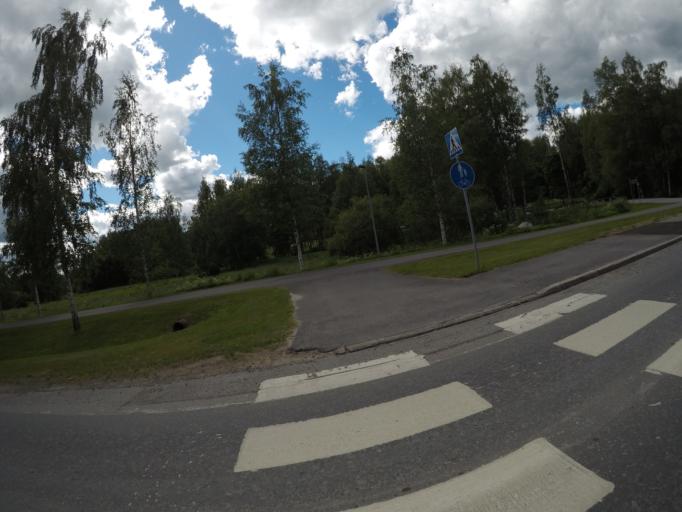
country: FI
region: Haeme
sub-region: Haemeenlinna
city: Haemeenlinna
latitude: 61.0060
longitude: 24.4531
